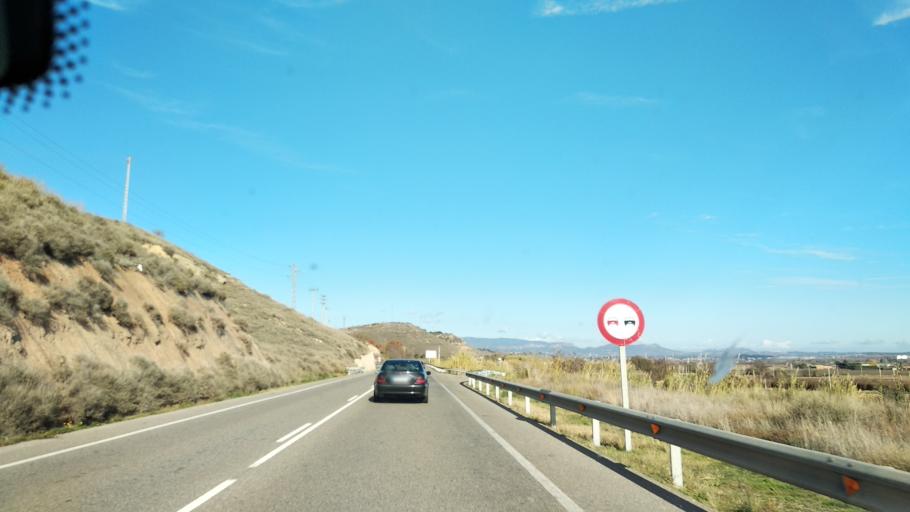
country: ES
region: Catalonia
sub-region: Provincia de Lleida
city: Termens
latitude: 41.7480
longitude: 0.7636
